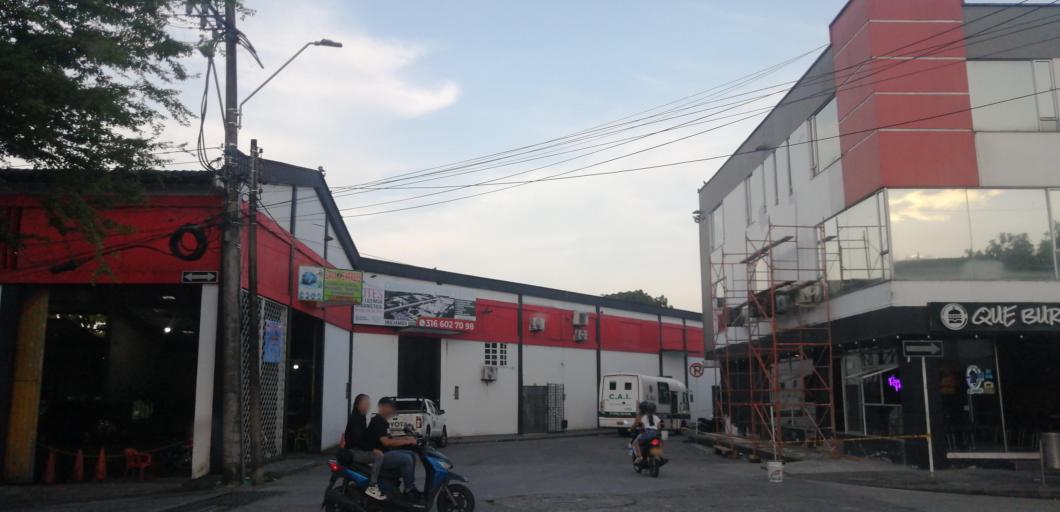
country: CO
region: Meta
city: Acacias
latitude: 3.9873
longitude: -73.7576
